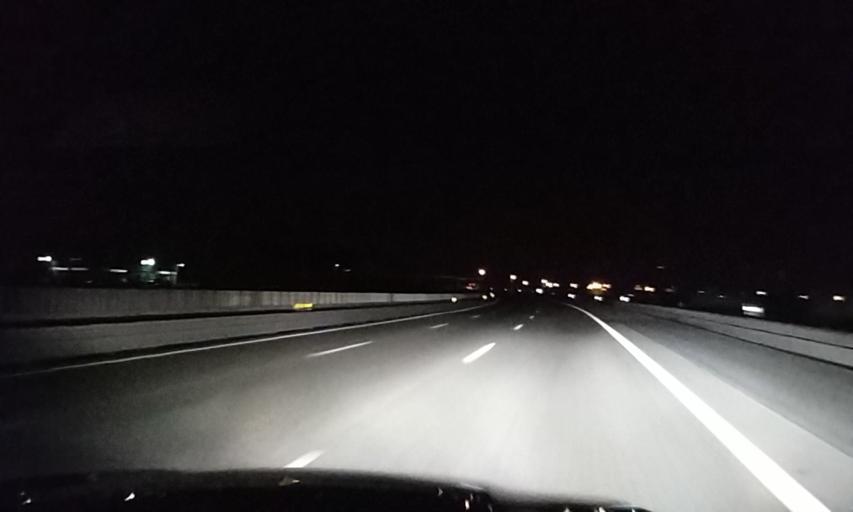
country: PT
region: Santarem
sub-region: Santarem
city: Santarem
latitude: 39.3309
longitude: -8.6563
